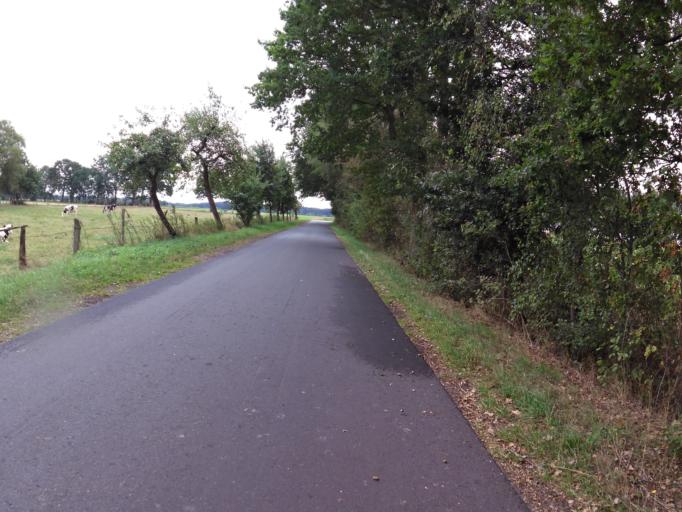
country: DE
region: Lower Saxony
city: Scheessel
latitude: 53.1950
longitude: 9.4644
